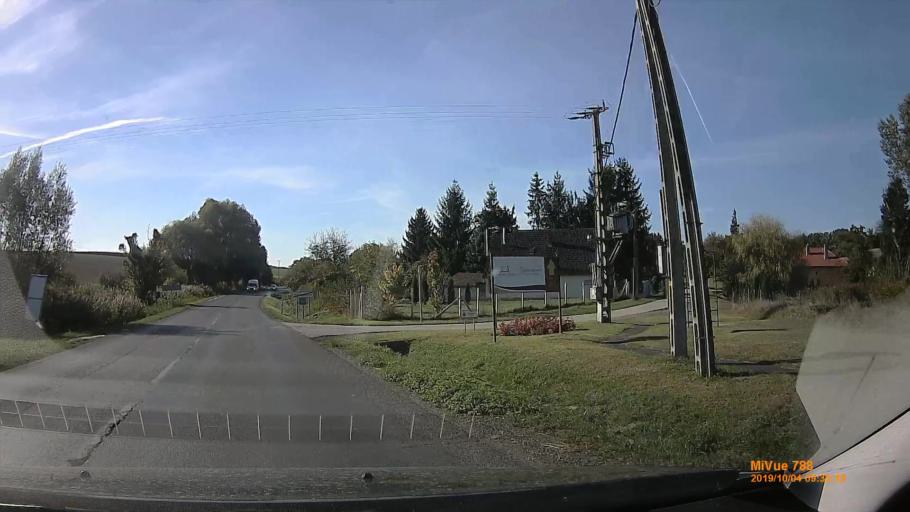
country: HU
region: Somogy
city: Kaposvar
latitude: 46.4517
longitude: 17.8044
